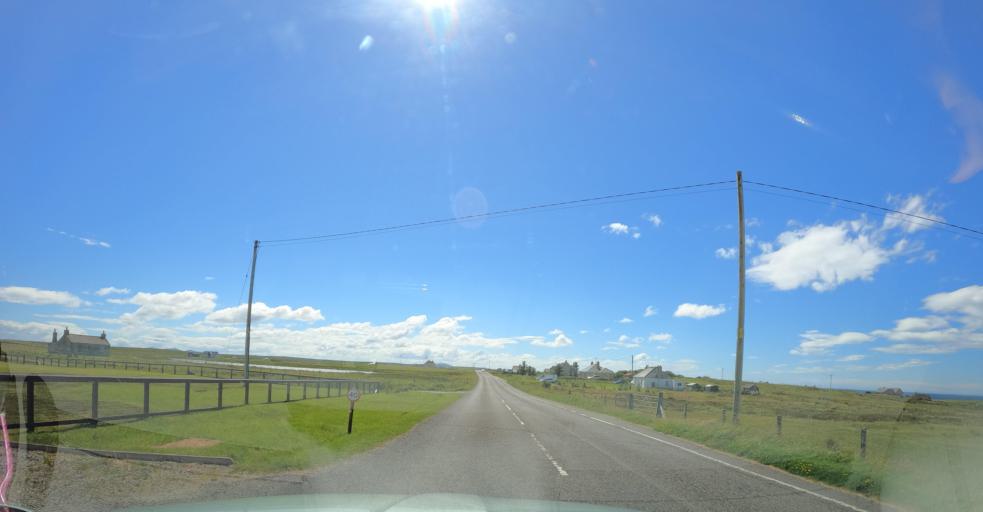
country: GB
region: Scotland
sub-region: Eilean Siar
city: Isle of Lewis
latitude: 58.4028
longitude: -6.4635
